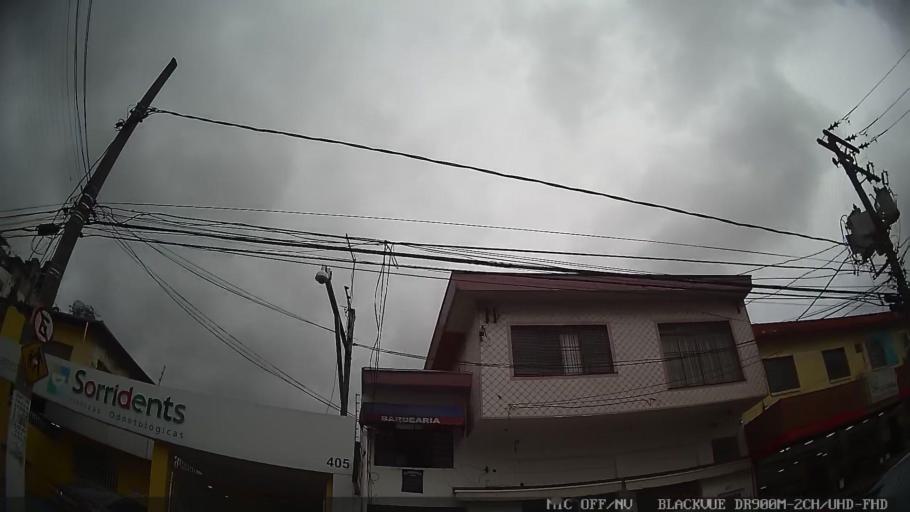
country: BR
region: Sao Paulo
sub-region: Osasco
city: Osasco
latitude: -23.4873
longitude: -46.7167
